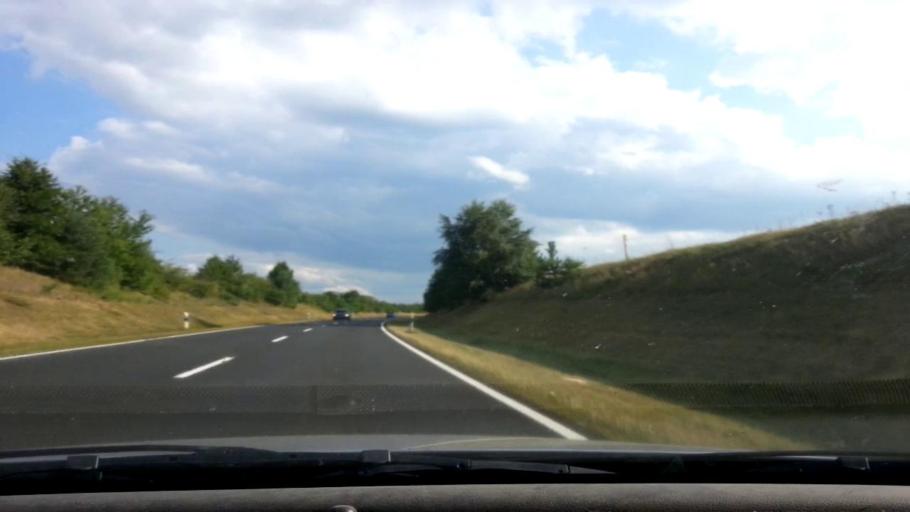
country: DE
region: Bavaria
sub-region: Upper Palatinate
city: Mitterteich
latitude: 49.9511
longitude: 12.2628
